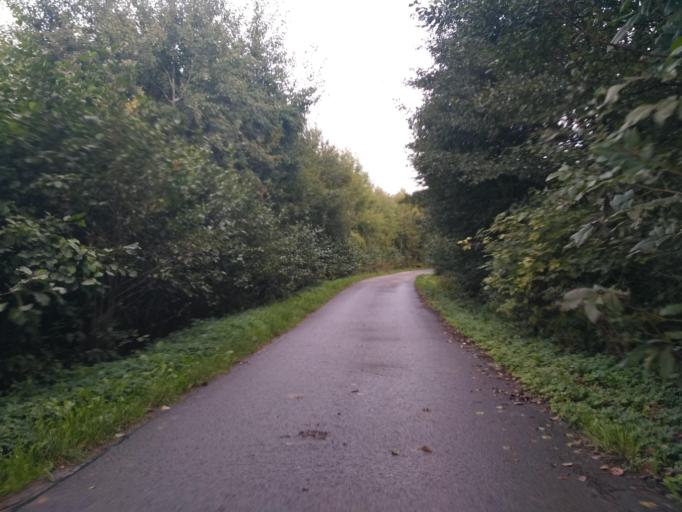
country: PL
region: Subcarpathian Voivodeship
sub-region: Powiat ropczycko-sedziszowski
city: Niedzwiada
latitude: 49.9413
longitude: 21.5066
